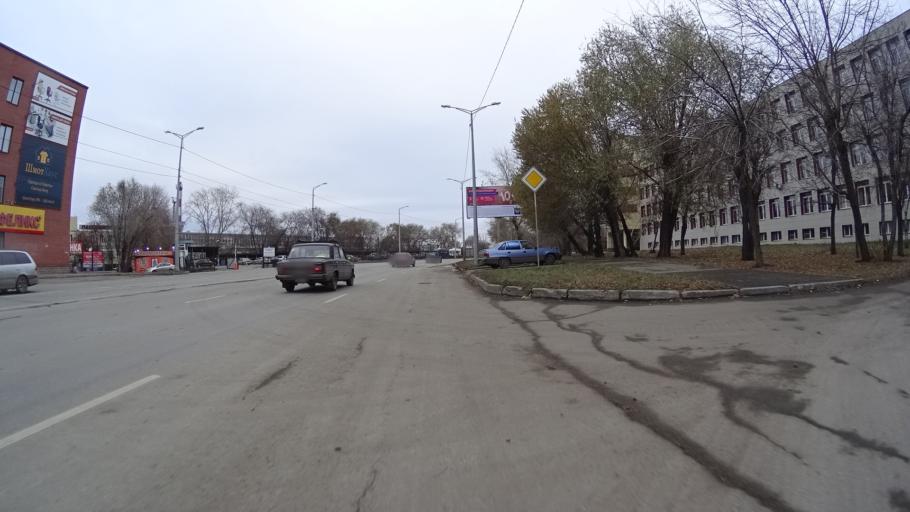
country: RU
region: Chelyabinsk
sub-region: Gorod Chelyabinsk
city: Chelyabinsk
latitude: 55.1542
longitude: 61.4186
